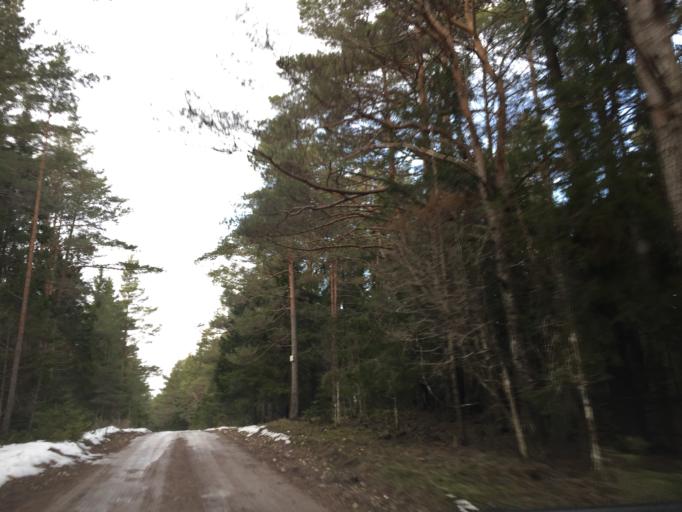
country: EE
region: Saare
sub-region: Kuressaare linn
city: Kuressaare
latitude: 58.4877
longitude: 21.9389
